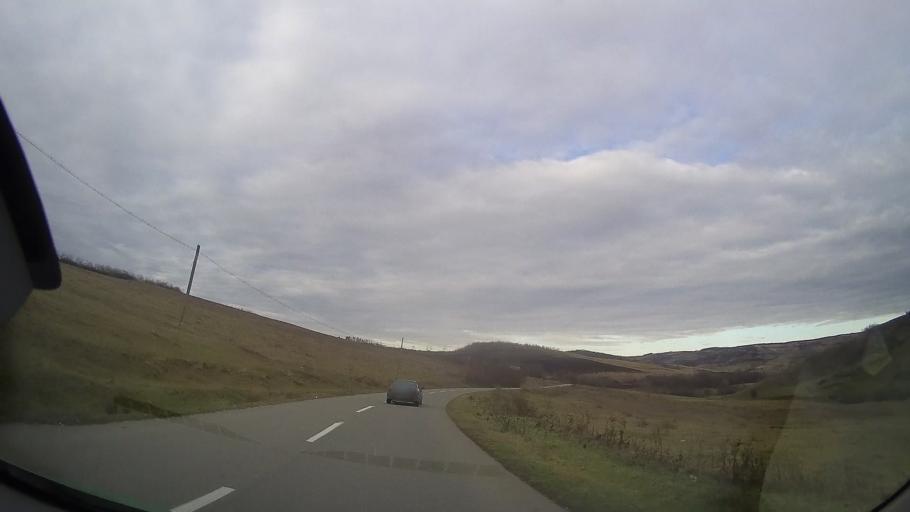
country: RO
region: Bistrita-Nasaud
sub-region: Comuna Milas
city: Milas
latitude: 46.8279
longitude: 24.4496
